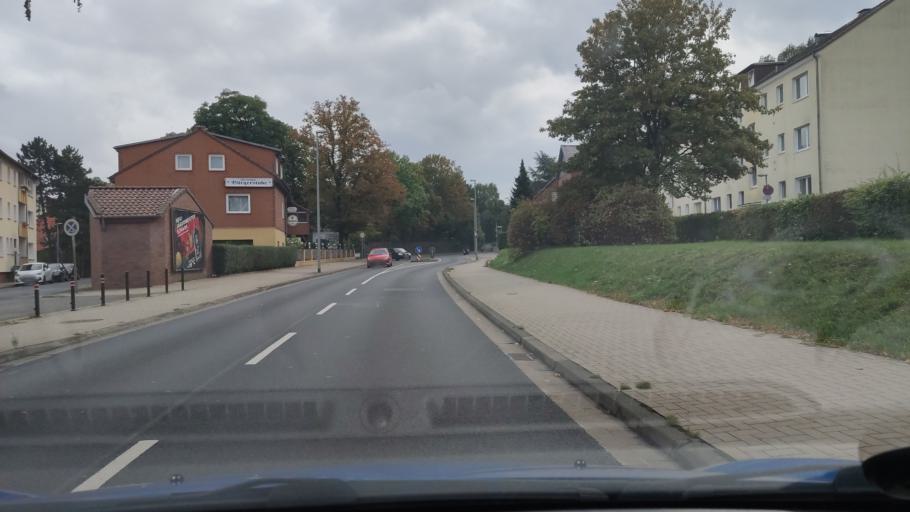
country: DE
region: Lower Saxony
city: Seelze
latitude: 52.3871
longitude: 9.6604
